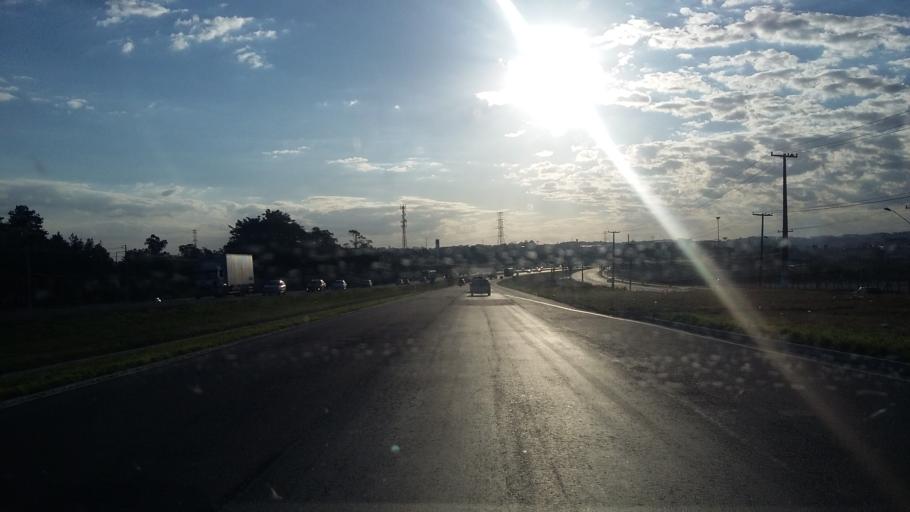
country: BR
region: Parana
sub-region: Araucaria
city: Araucaria
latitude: -25.5321
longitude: -49.3219
